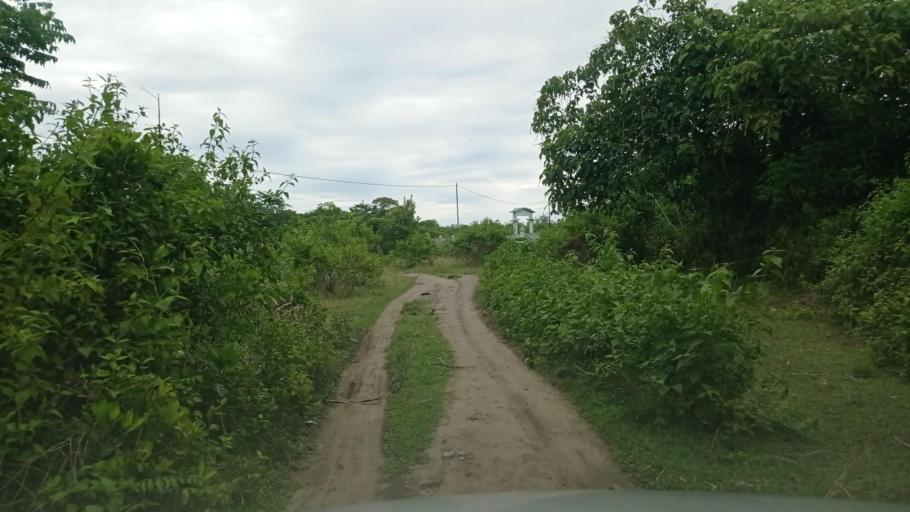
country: ID
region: Jambi
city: Sungai Penuh
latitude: -2.5172
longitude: 101.0640
